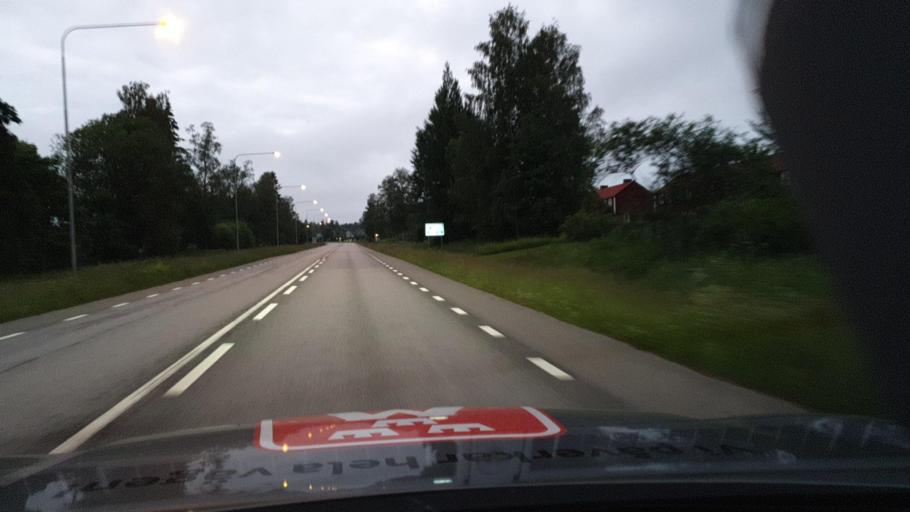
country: SE
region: OErebro
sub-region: Hallefors Kommun
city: Haellefors
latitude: 59.7786
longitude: 14.5276
